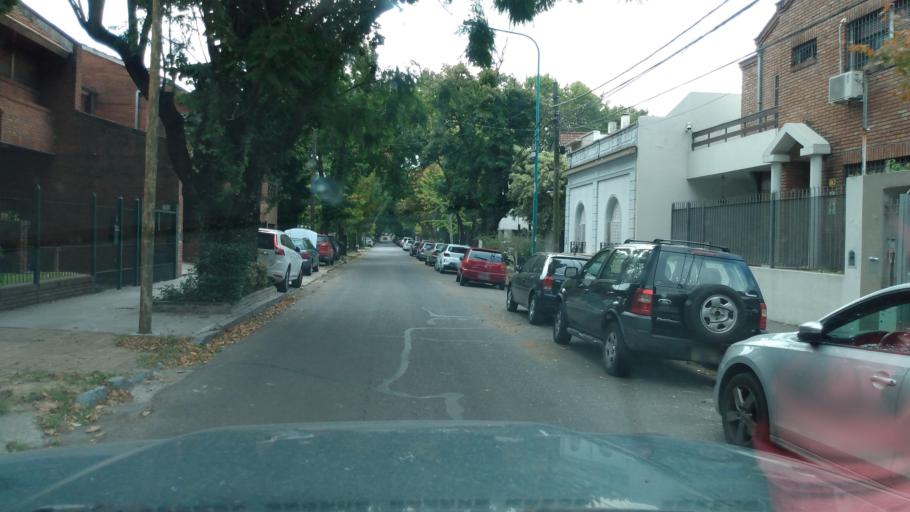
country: AR
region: Buenos Aires
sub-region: Partido de Vicente Lopez
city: Olivos
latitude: -34.5170
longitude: -58.4932
